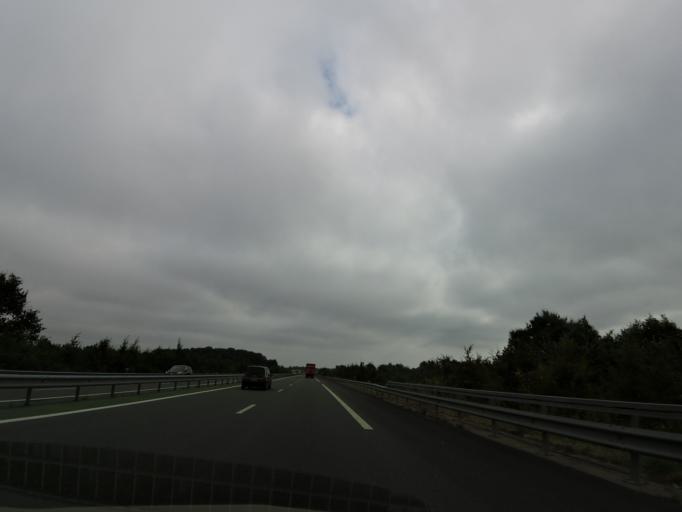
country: FR
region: Pays de la Loire
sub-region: Departement de la Vendee
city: La Ferriere
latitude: 46.6810
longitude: -1.3310
